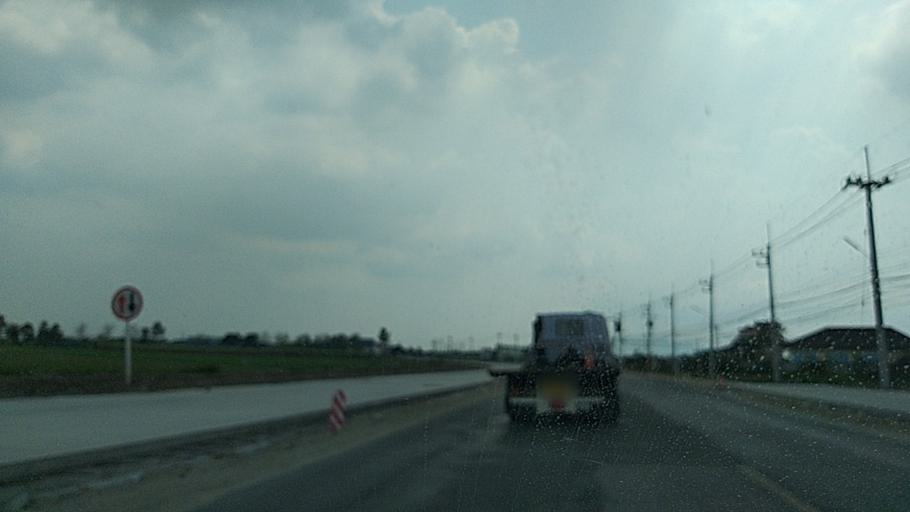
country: TH
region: Chon Buri
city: Ban Bueng
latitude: 13.3021
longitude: 101.1784
